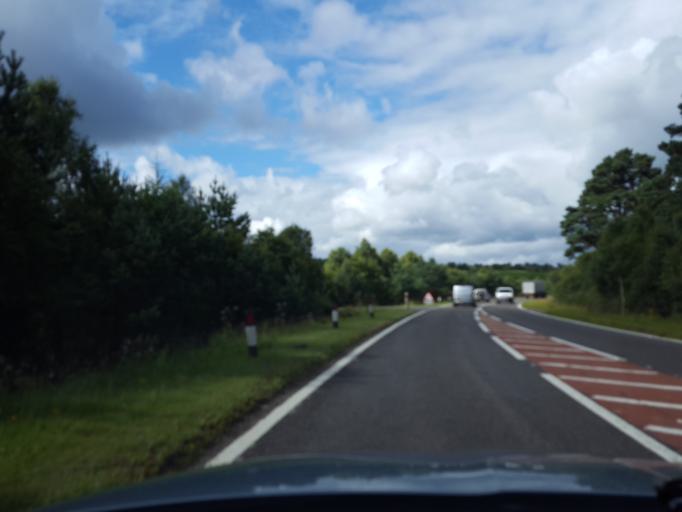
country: GB
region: Scotland
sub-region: Highland
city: Grantown on Spey
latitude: 57.3159
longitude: -3.5923
